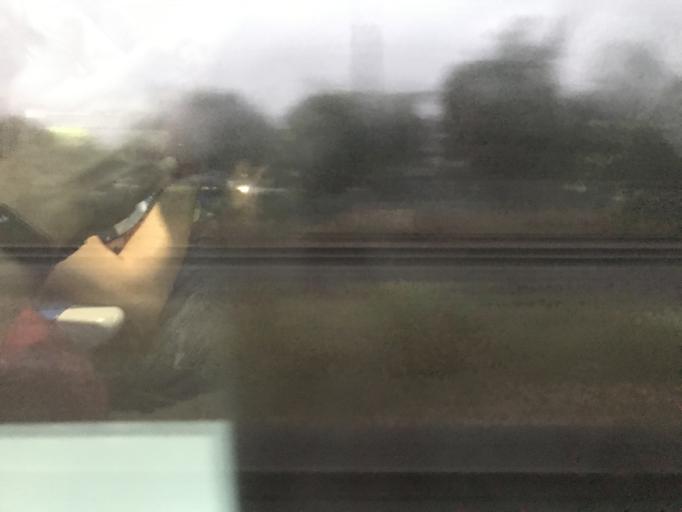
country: TR
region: Kocaeli
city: Korfez
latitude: 40.7725
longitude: 29.7292
